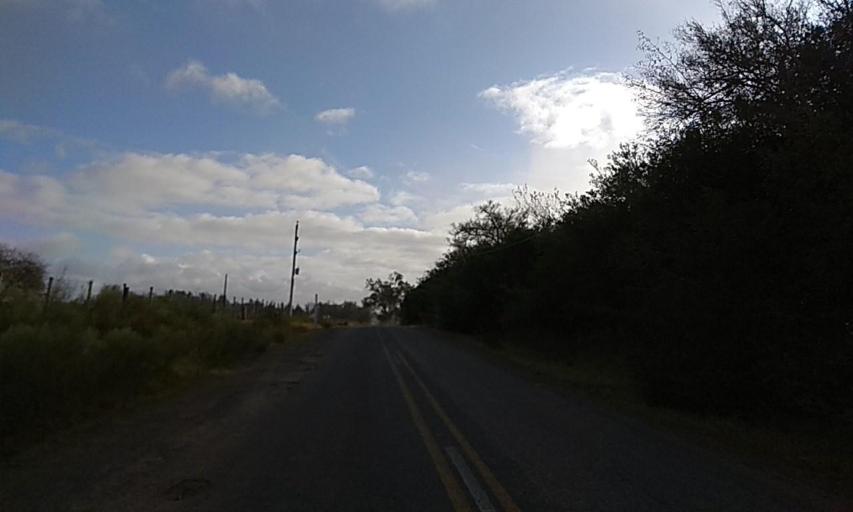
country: UY
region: Florida
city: Florida
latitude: -34.0537
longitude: -56.1899
